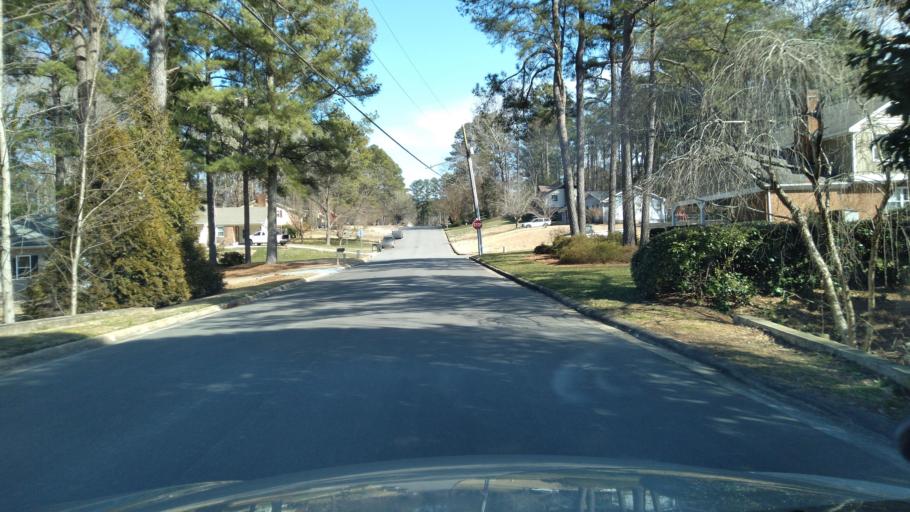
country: US
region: North Carolina
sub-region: Wake County
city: Garner
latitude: 35.6961
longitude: -78.6281
